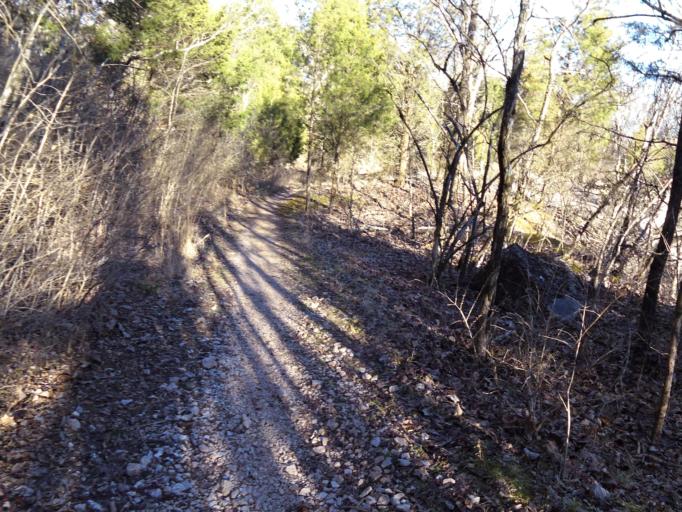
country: US
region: Tennessee
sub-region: Knox County
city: Knoxville
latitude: 35.9454
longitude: -83.8753
